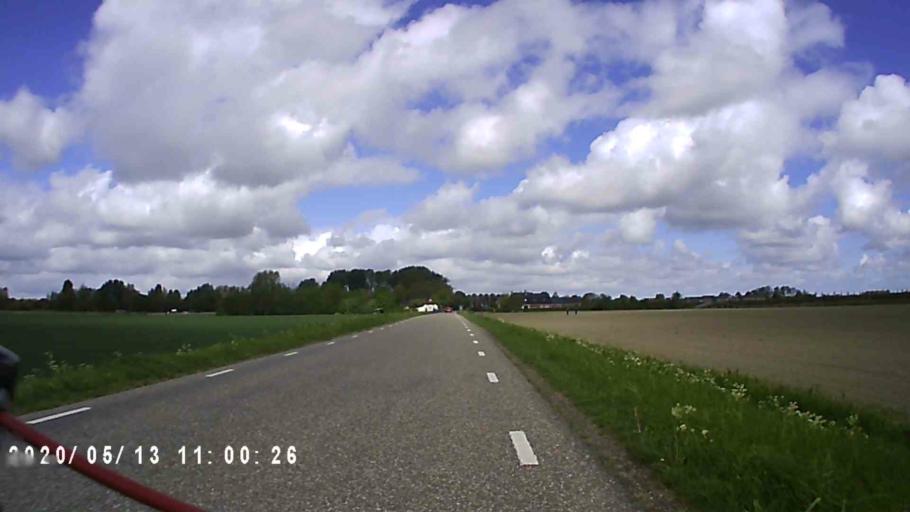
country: NL
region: Groningen
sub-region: Gemeente Zuidhorn
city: Grijpskerk
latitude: 53.2793
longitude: 6.3293
